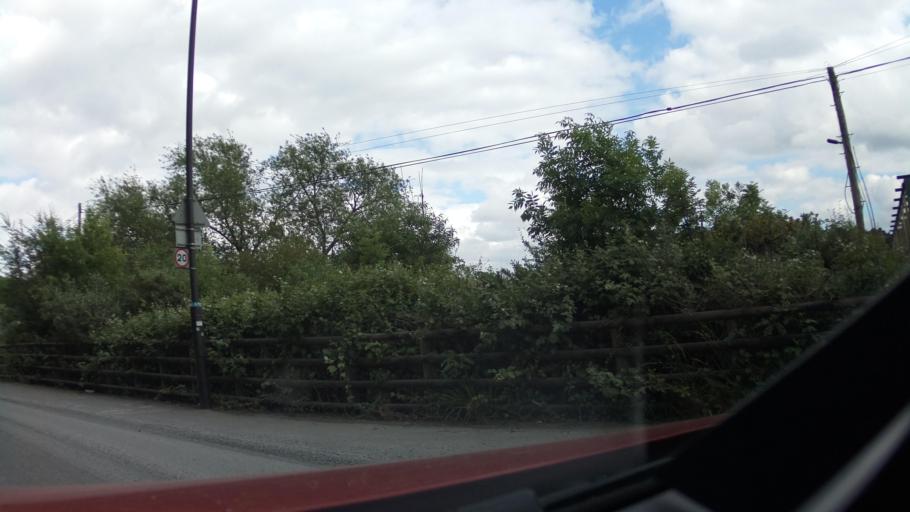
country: GB
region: England
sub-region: South Gloucestershire
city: Kingswood
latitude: 51.4549
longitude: -2.5472
